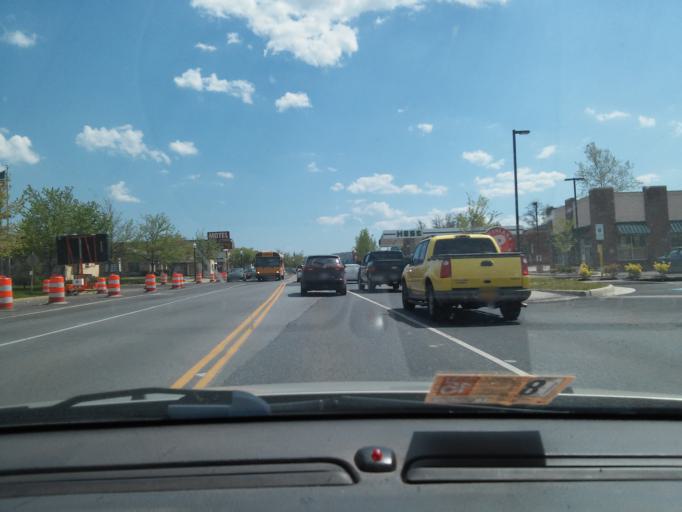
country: US
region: Virginia
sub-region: Warren County
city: Front Royal
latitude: 38.9384
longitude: -78.1994
